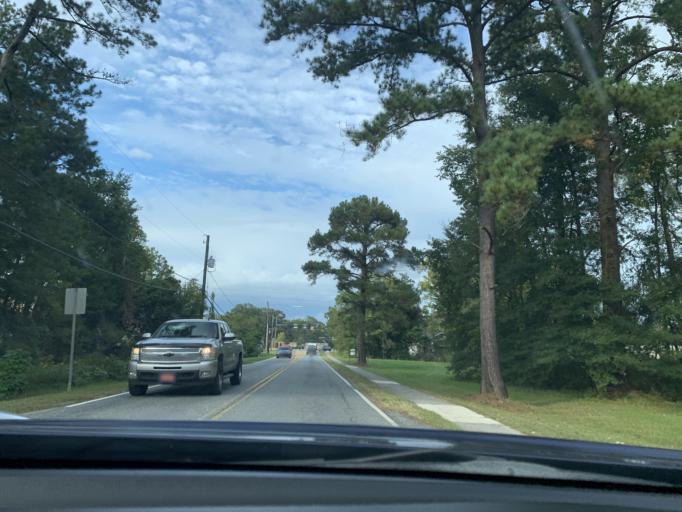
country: US
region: Georgia
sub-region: Chatham County
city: Pooler
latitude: 32.1137
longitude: -81.2495
